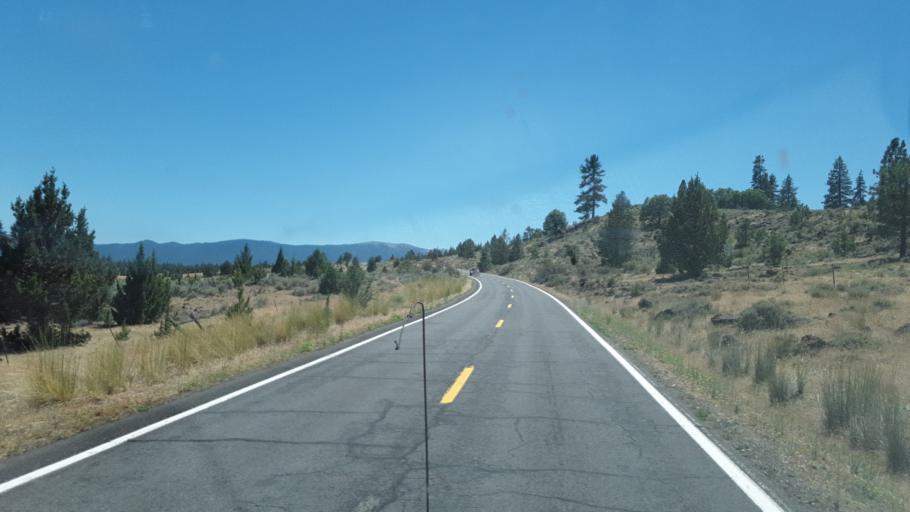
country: US
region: California
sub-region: Lassen County
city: Susanville
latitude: 40.4559
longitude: -120.6208
